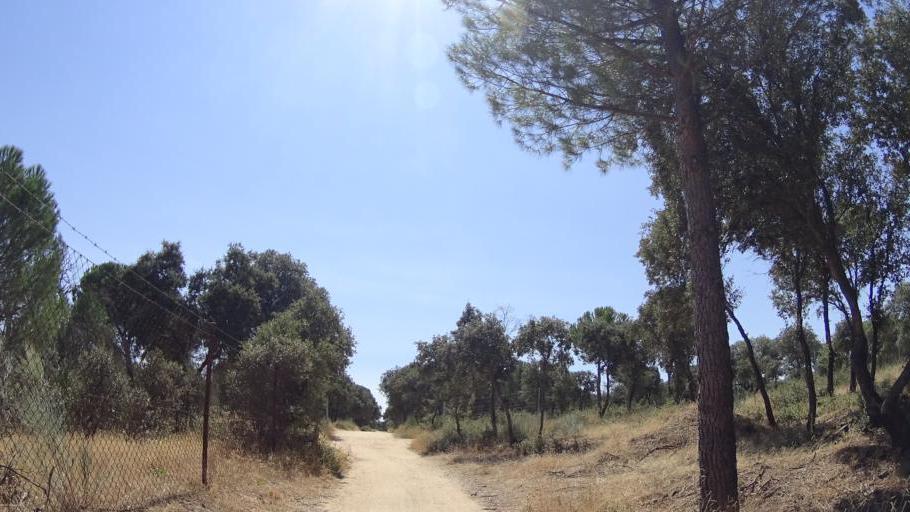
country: ES
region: Madrid
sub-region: Provincia de Madrid
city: Majadahonda
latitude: 40.4411
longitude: -3.8637
